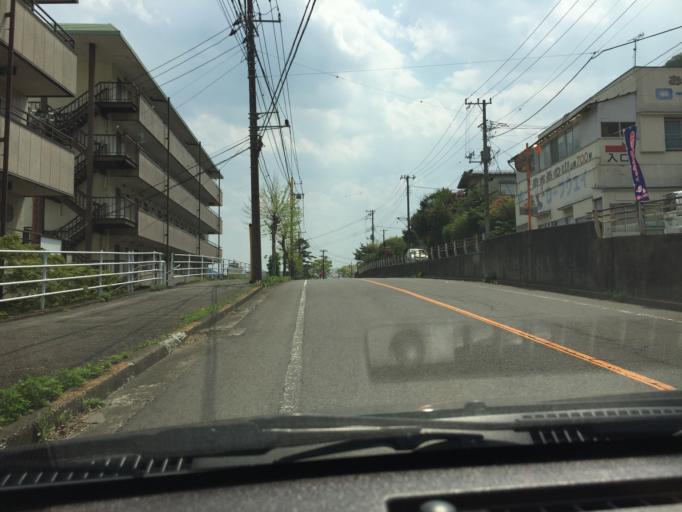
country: JP
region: Tochigi
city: Imaichi
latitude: 36.8368
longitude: 139.7190
